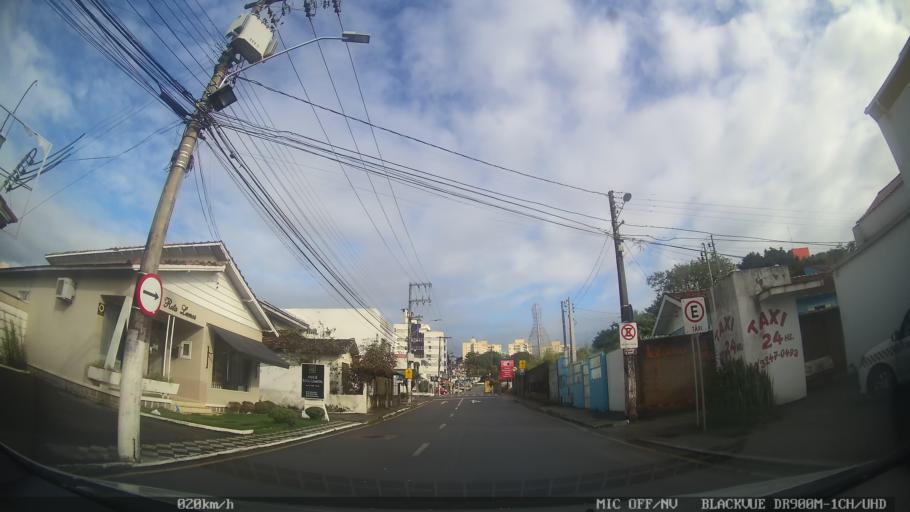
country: BR
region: Santa Catarina
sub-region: Sao Jose
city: Campinas
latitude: -27.6075
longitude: -48.6279
